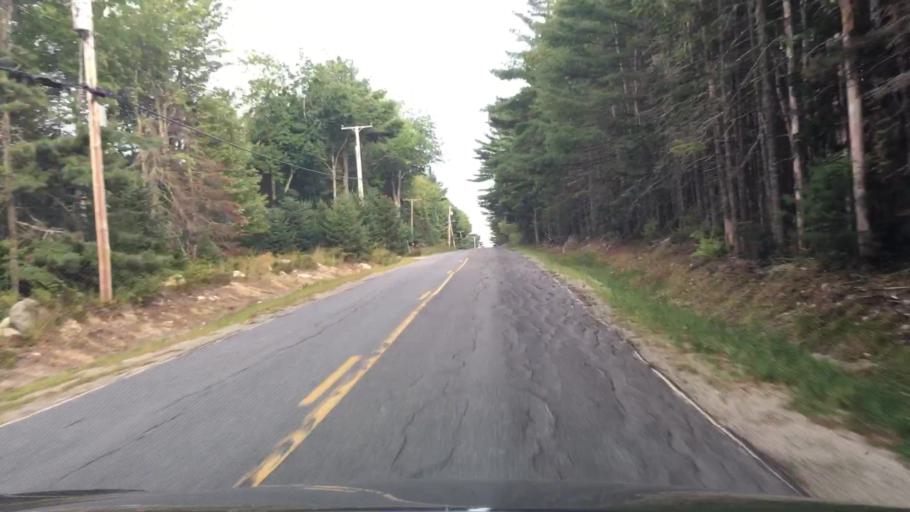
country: US
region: Maine
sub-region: Hancock County
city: Surry
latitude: 44.4999
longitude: -68.5590
